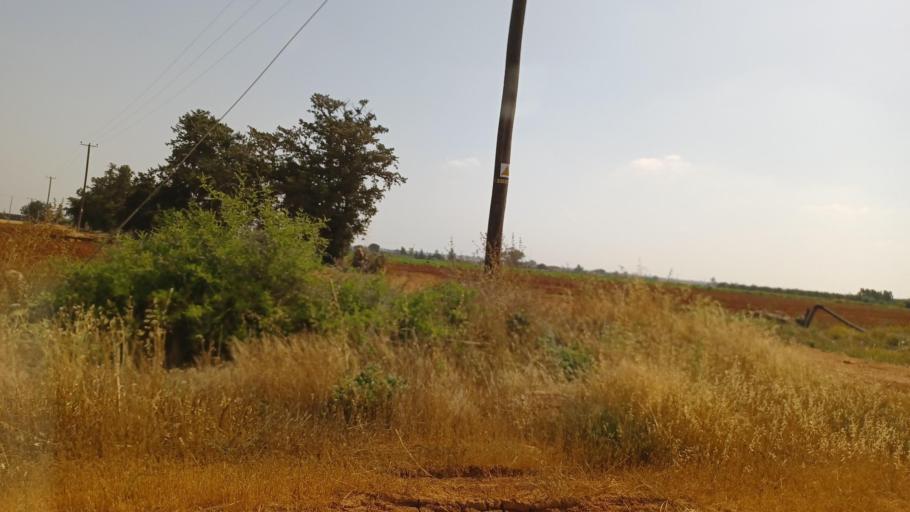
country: CY
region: Ammochostos
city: Avgorou
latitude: 35.0607
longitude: 33.8626
